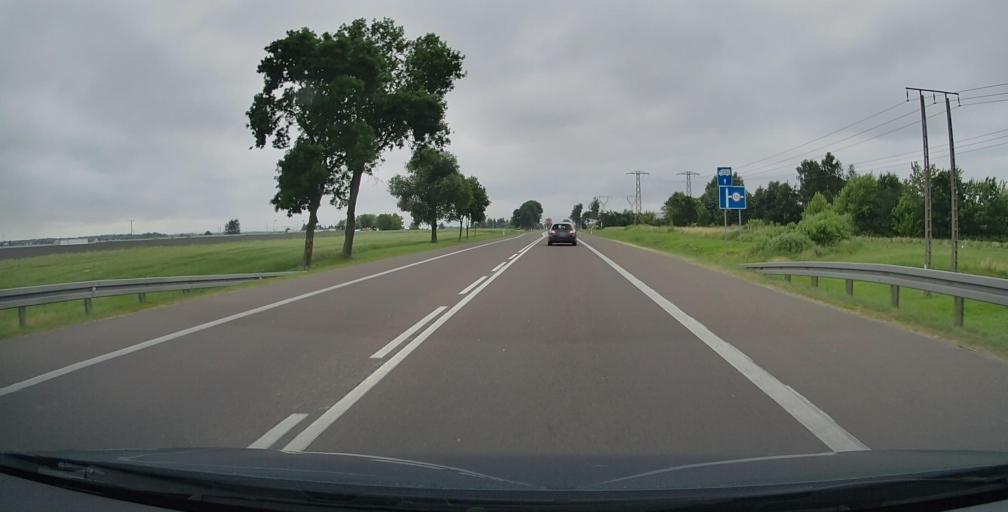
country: PL
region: Lublin Voivodeship
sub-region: Powiat bialski
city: Miedzyrzec Podlaski
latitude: 52.0002
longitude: 22.7747
